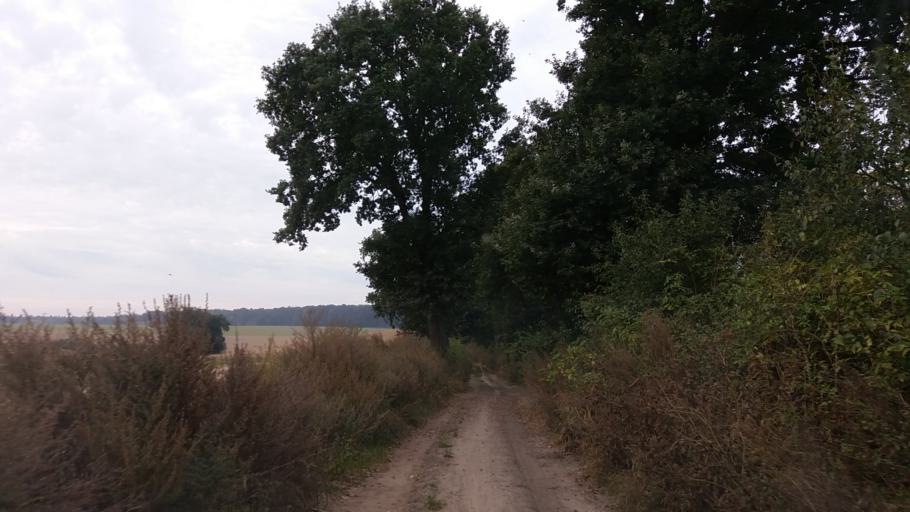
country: PL
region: West Pomeranian Voivodeship
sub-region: Powiat choszczenski
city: Pelczyce
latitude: 53.0831
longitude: 15.2960
